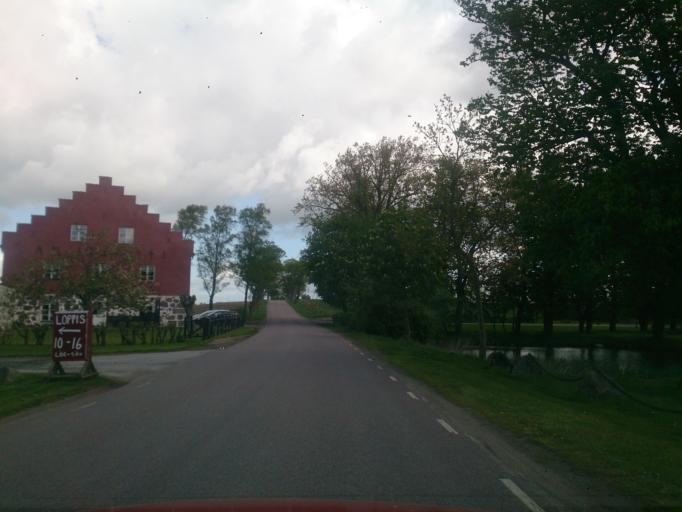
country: SE
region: Skane
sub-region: Ystads Kommun
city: Ystad
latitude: 55.4636
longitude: 13.7056
